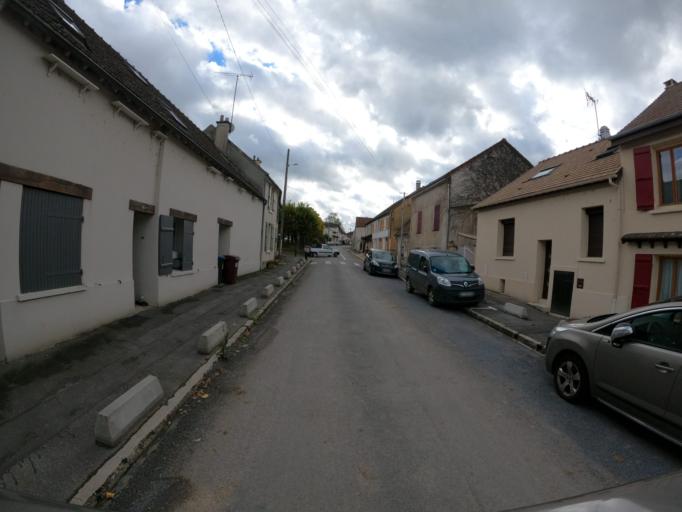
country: FR
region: Ile-de-France
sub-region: Departement de Seine-et-Marne
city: Chalifert
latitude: 48.9186
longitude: 2.7638
